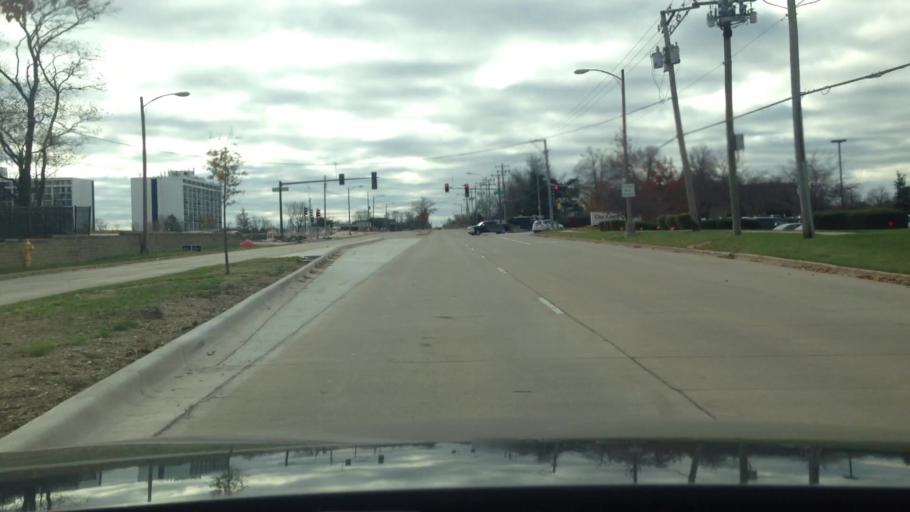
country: US
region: Illinois
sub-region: DuPage County
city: Lombard
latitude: 41.8512
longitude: -88.0266
